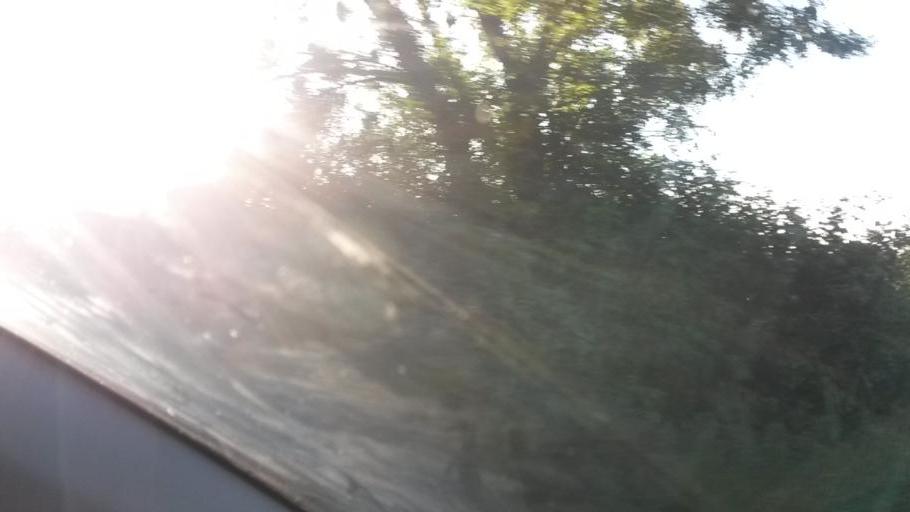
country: IE
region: Leinster
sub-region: An Mhi
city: Ashbourne
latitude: 53.5738
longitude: -6.3797
